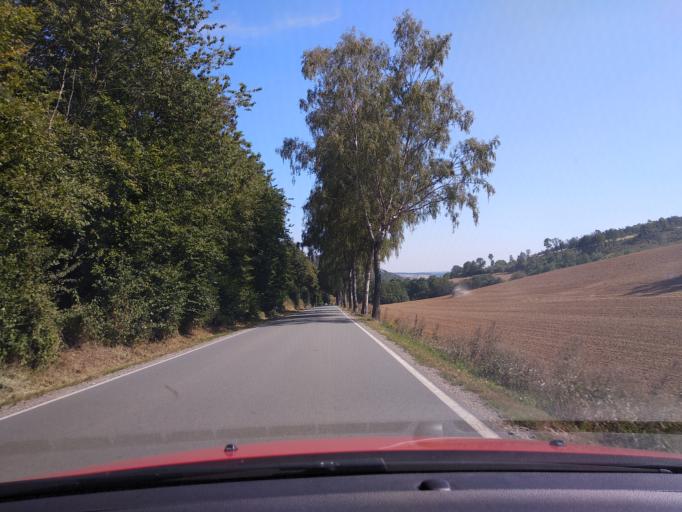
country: DE
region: North Rhine-Westphalia
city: Beverungen
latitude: 51.6821
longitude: 9.3353
